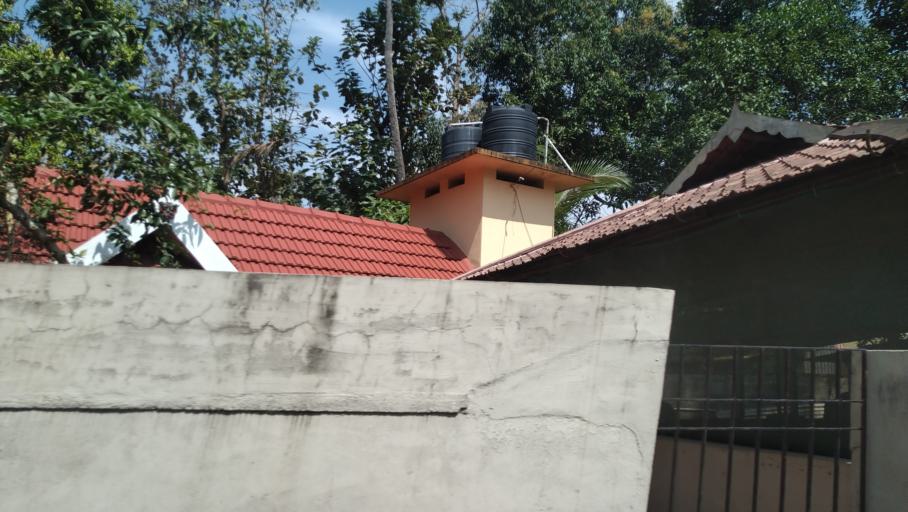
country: IN
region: Kerala
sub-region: Ernakulam
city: Aluva
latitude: 10.1254
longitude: 76.3526
